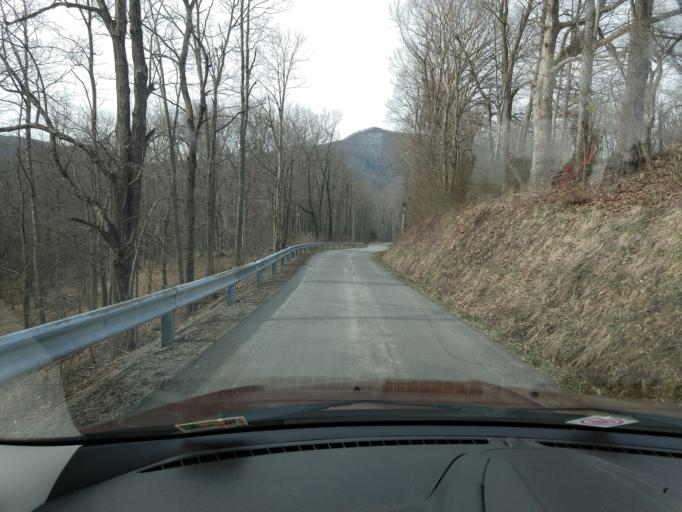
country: US
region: West Virginia
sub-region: Tucker County
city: Parsons
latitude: 39.0254
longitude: -79.5635
